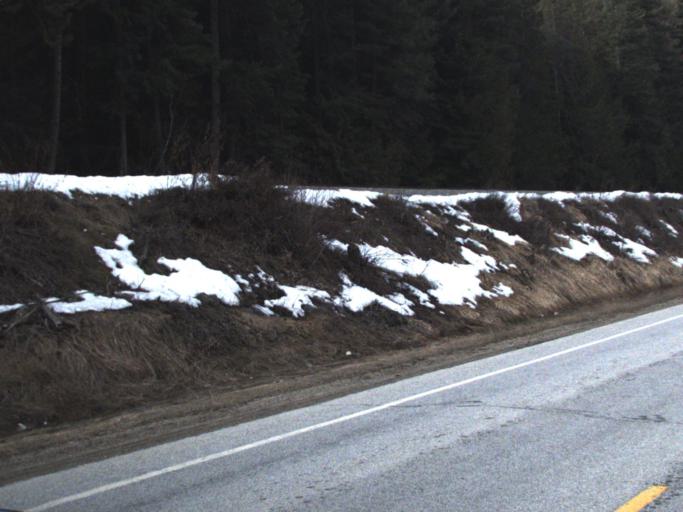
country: US
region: Washington
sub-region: Pend Oreille County
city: Newport
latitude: 48.2307
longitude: -117.1935
